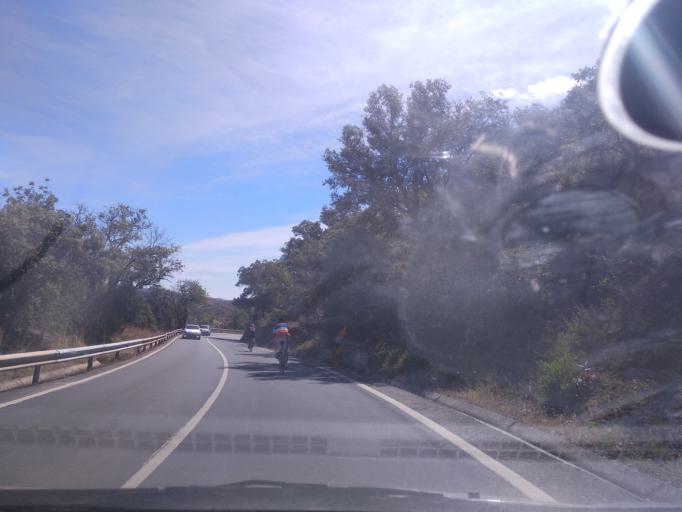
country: PT
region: Faro
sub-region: Sao Bras de Alportel
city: Sao Bras de Alportel
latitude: 37.1555
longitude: -7.8426
